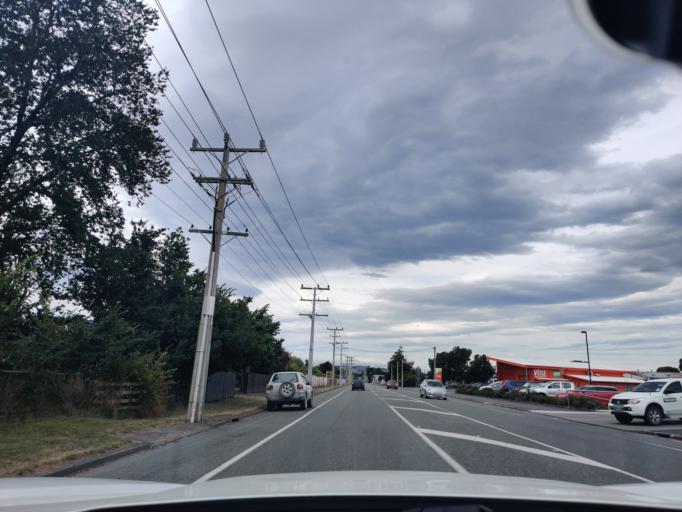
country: NZ
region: Wellington
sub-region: Masterton District
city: Masterton
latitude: -40.9480
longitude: 175.6348
